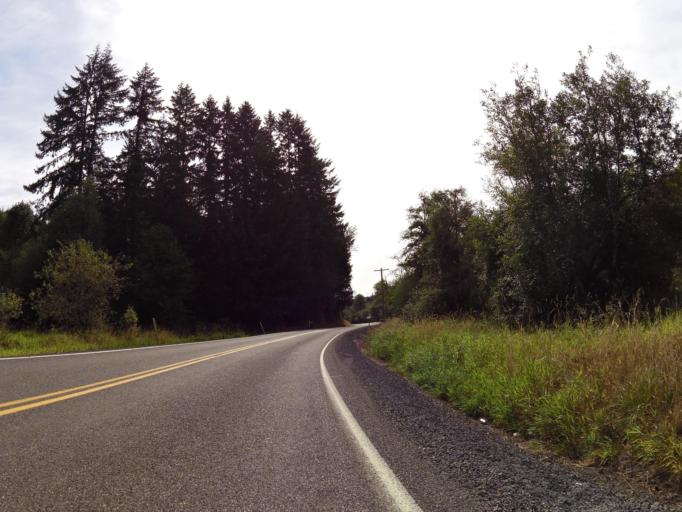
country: US
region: Washington
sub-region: Lewis County
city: Napavine
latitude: 46.5706
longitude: -122.9683
